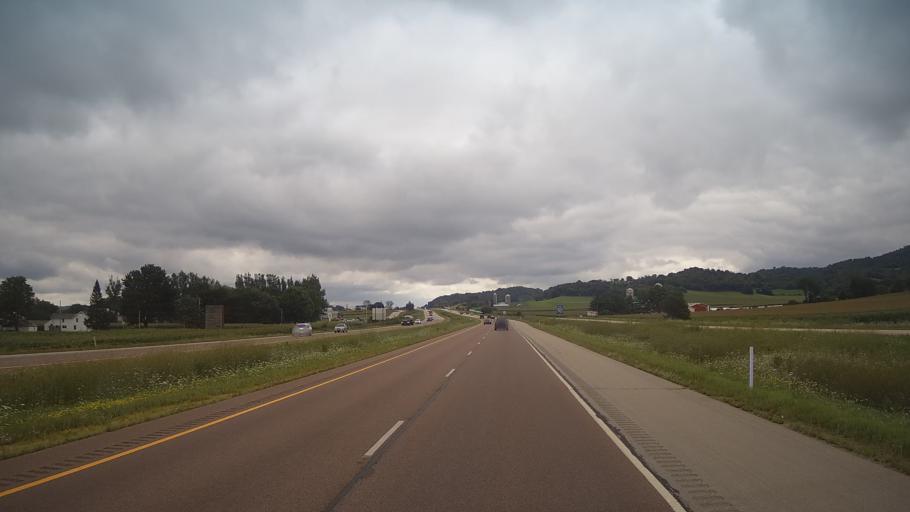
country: US
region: Wisconsin
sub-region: La Crosse County
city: West Salem
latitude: 43.8915
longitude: -91.0663
